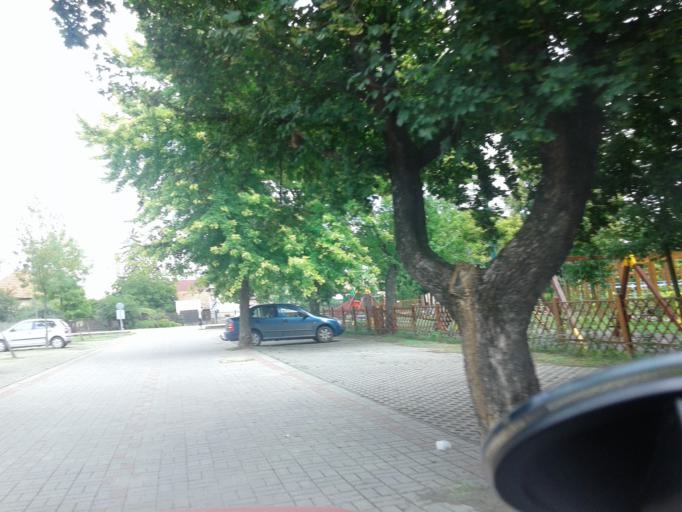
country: HU
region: Csongrad
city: Morahalom
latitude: 46.2170
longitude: 19.8906
